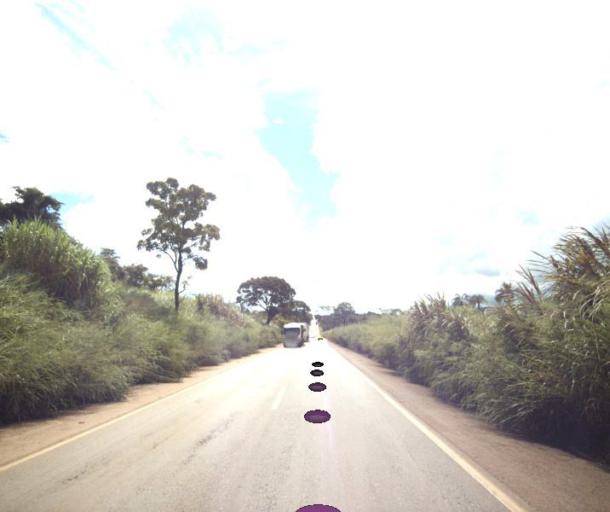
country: BR
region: Goias
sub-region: Petrolina De Goias
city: Petrolina de Goias
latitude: -15.9889
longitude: -49.1535
